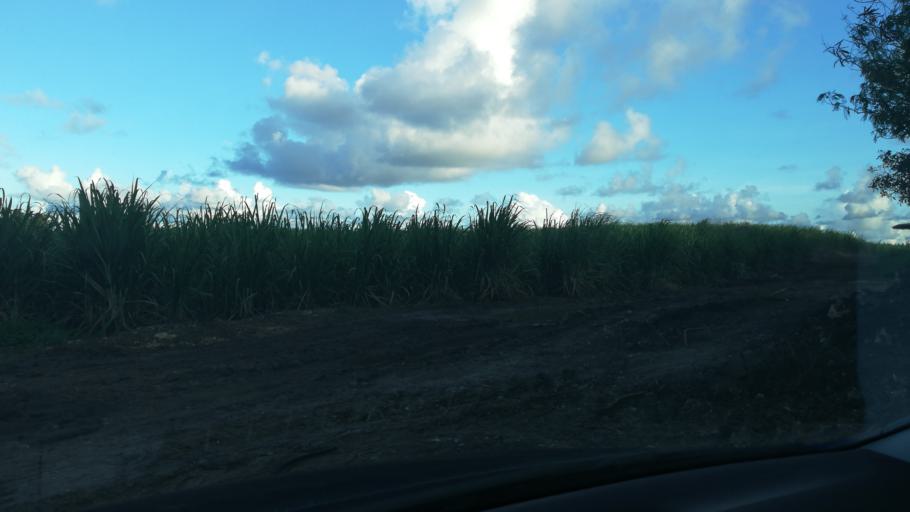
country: GP
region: Guadeloupe
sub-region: Guadeloupe
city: Petit-Canal
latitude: 16.3760
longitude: -61.4255
